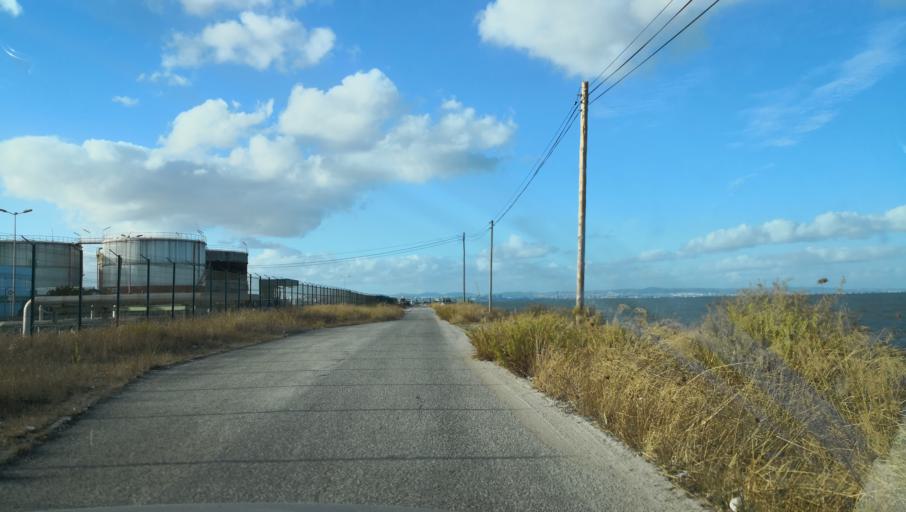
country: PT
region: Setubal
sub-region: Barreiro
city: Barreiro
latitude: 38.6812
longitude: -9.0567
